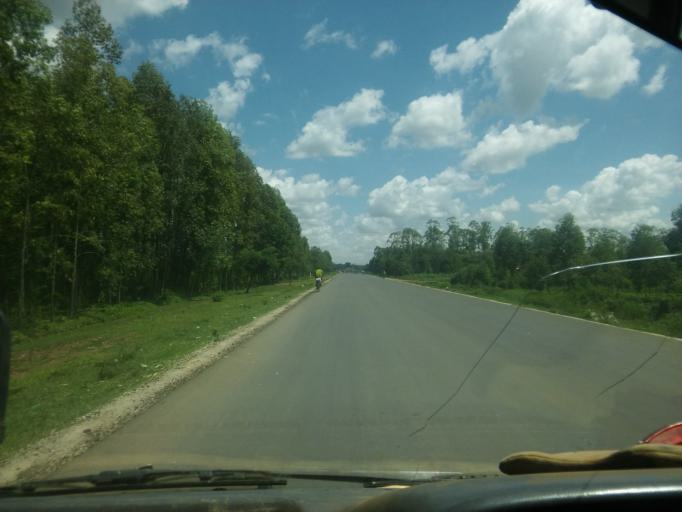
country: UG
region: Eastern Region
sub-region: Mbale District
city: Mbale
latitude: 1.0759
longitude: 34.1343
